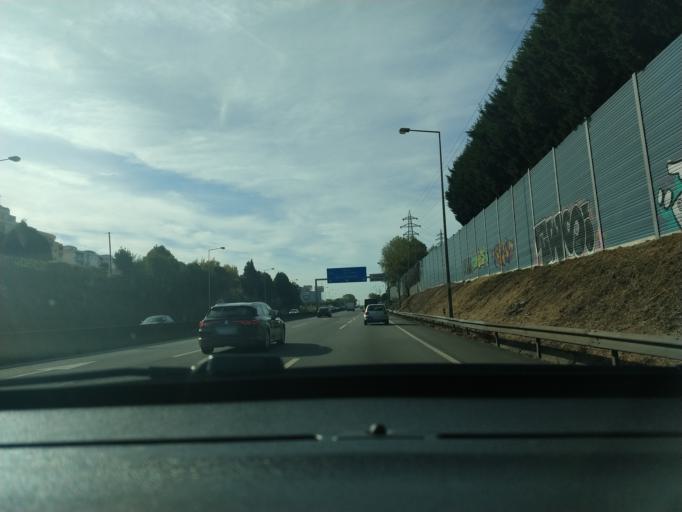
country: PT
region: Porto
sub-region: Vila Nova de Gaia
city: Canidelo
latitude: 41.1307
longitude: -8.6357
